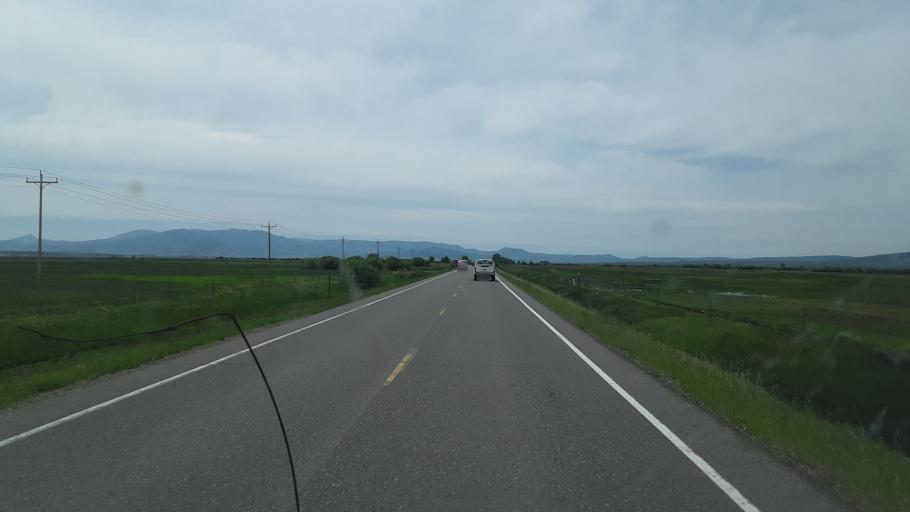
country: US
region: Colorado
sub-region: Jackson County
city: Walden
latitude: 40.6047
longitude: -106.4069
